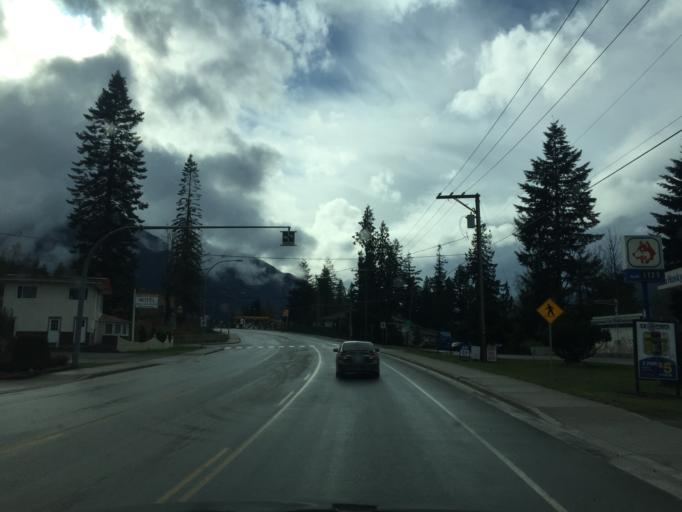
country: CA
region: British Columbia
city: Hope
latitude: 49.3751
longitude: -121.4365
